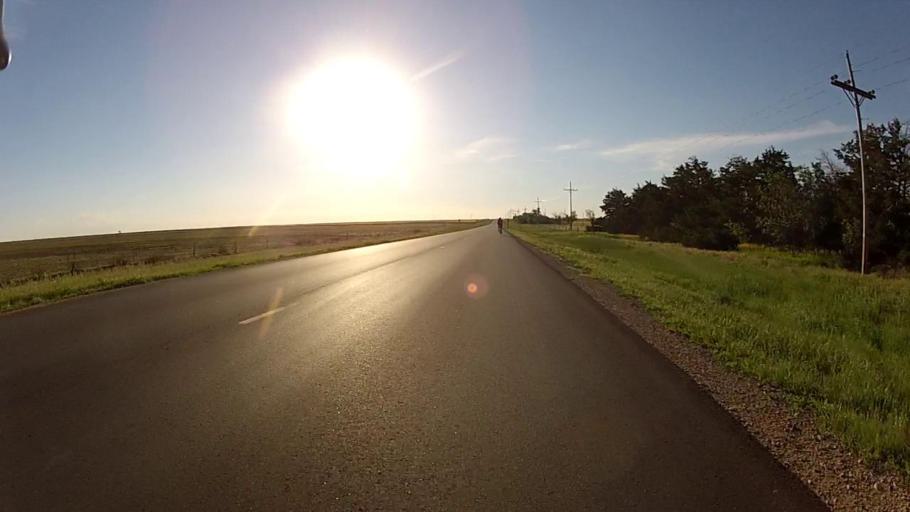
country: US
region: Kansas
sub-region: Comanche County
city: Coldwater
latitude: 37.2816
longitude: -99.1710
